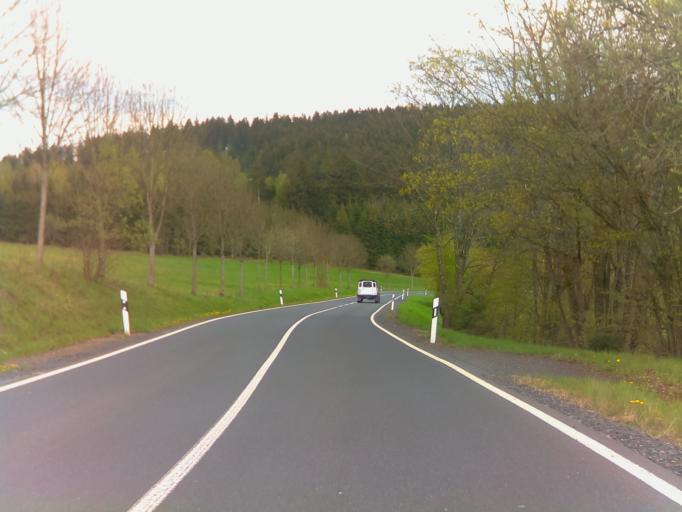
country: DE
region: Bavaria
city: Foritz
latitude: 50.3703
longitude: 11.2530
